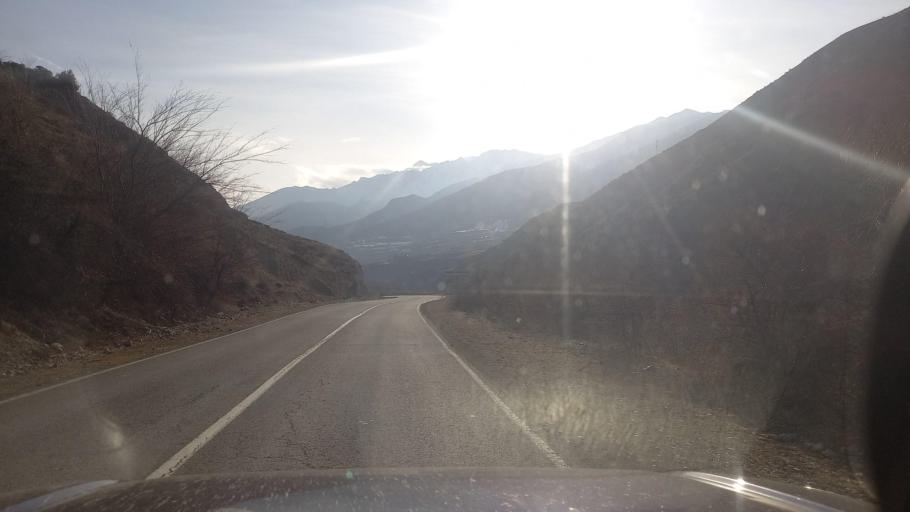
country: RU
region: Ingushetiya
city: Dzhayrakh
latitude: 42.8418
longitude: 44.6558
